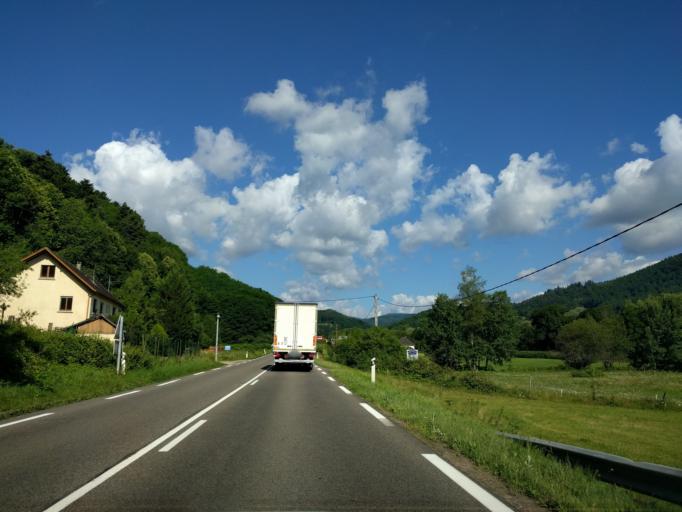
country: FR
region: Alsace
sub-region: Departement du Haut-Rhin
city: Liepvre
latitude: 48.2677
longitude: 7.2969
